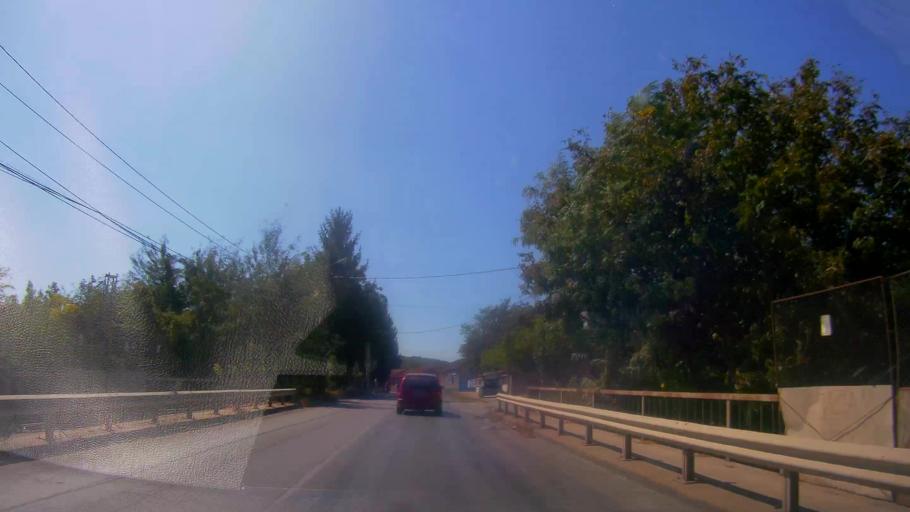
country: BG
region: Veliko Turnovo
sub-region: Obshtina Gorna Oryakhovitsa
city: Purvomaytsi
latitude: 43.1449
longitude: 25.6120
